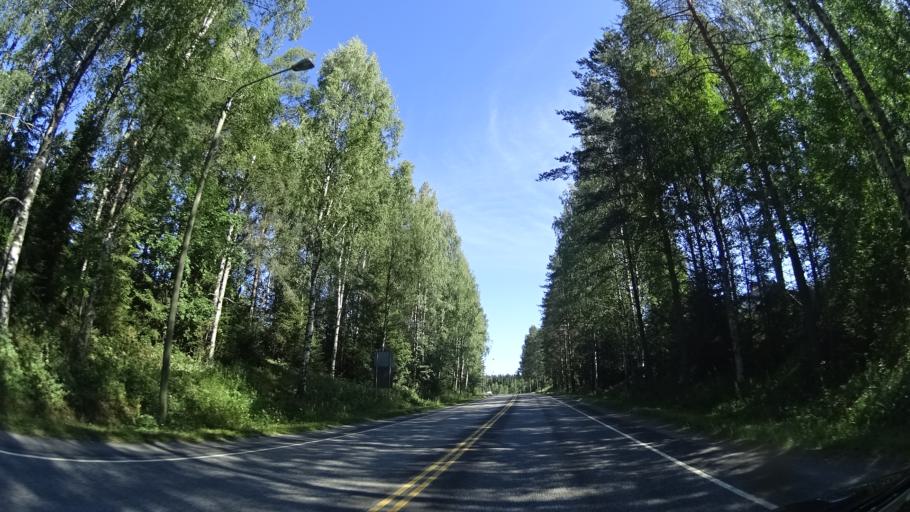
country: FI
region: Central Finland
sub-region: AEaenekoski
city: AEaenekoski
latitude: 62.8261
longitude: 25.8113
